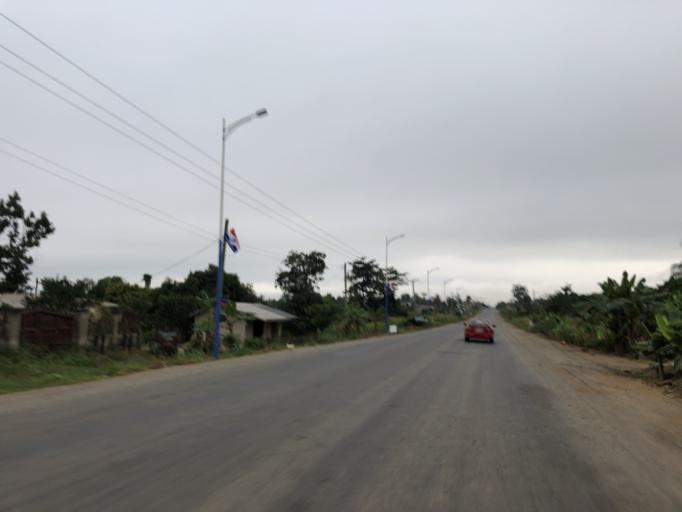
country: GH
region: Eastern
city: Koforidua
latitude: 6.1844
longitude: -0.3512
